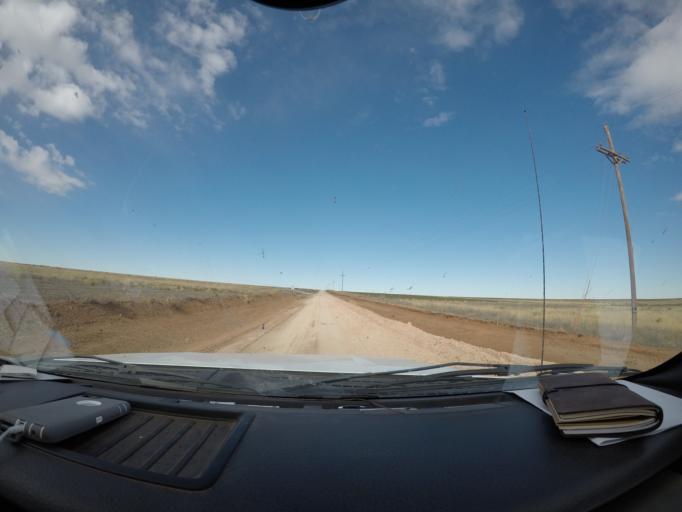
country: US
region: New Mexico
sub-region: Curry County
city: Texico
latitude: 34.6048
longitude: -103.0912
